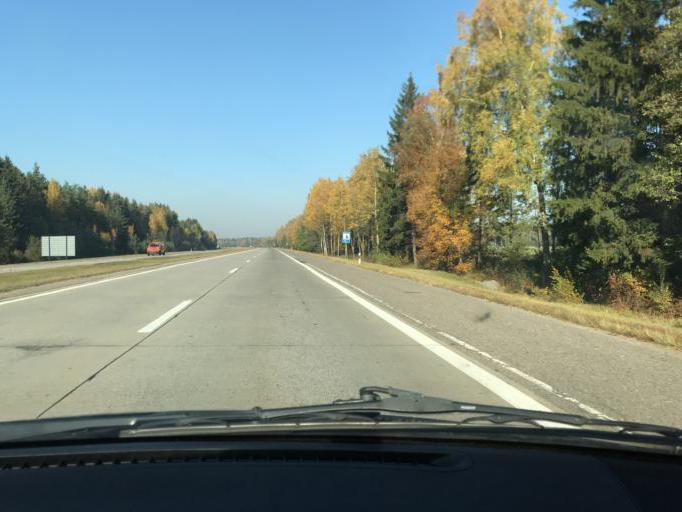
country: BY
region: Minsk
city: Uzda
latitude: 53.3636
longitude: 27.5102
